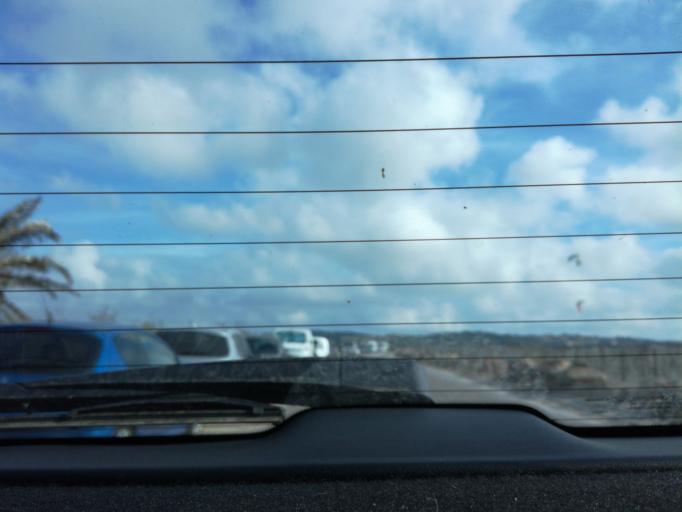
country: FR
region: Provence-Alpes-Cote d'Azur
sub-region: Departement du Var
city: Hyeres
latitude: 43.0581
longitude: 6.1333
